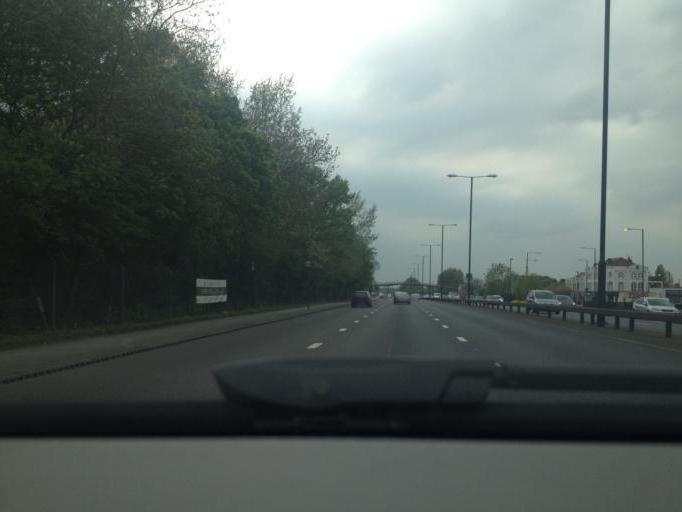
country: GB
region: England
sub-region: Greater London
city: Ealing Broadway
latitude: 51.5328
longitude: -0.3184
